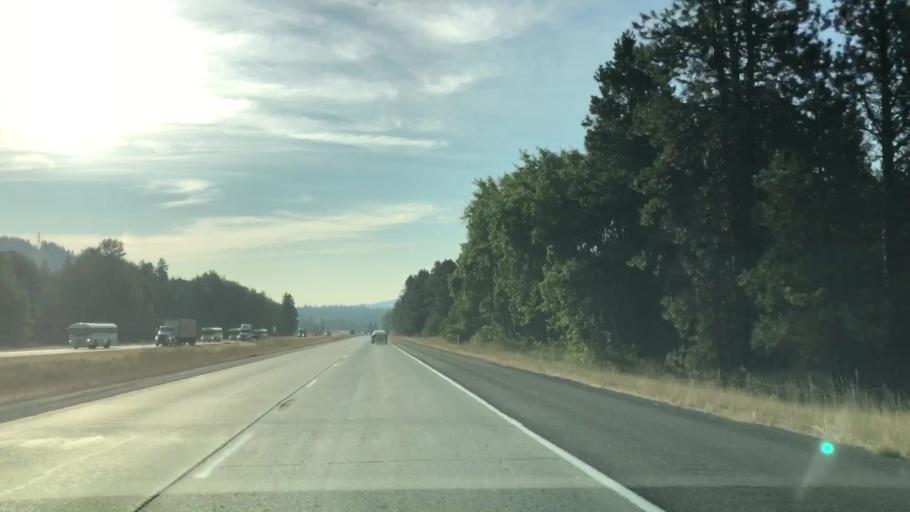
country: US
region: Washington
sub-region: Kittitas County
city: Cle Elum
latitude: 47.1996
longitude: -121.0686
